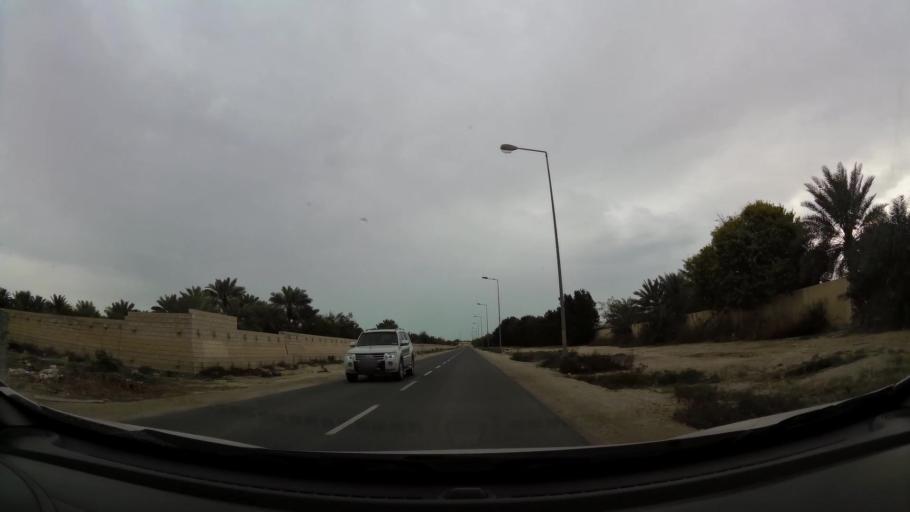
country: BH
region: Central Governorate
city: Madinat Hamad
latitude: 26.1498
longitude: 50.4661
